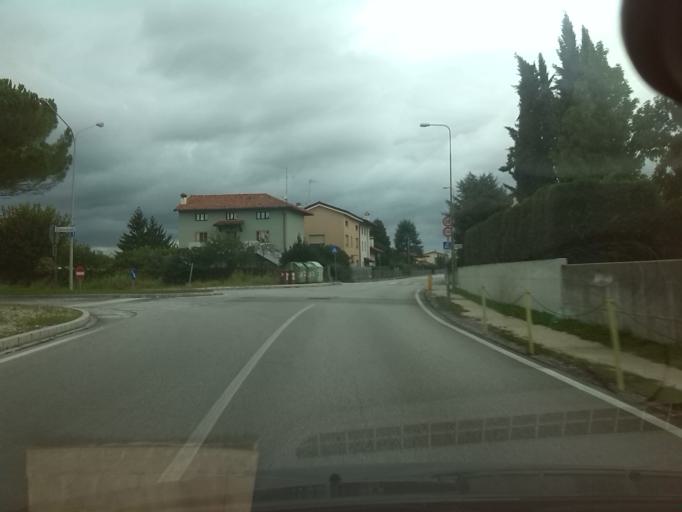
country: IT
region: Friuli Venezia Giulia
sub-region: Provincia di Udine
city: Udine
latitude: 46.0783
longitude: 13.2763
